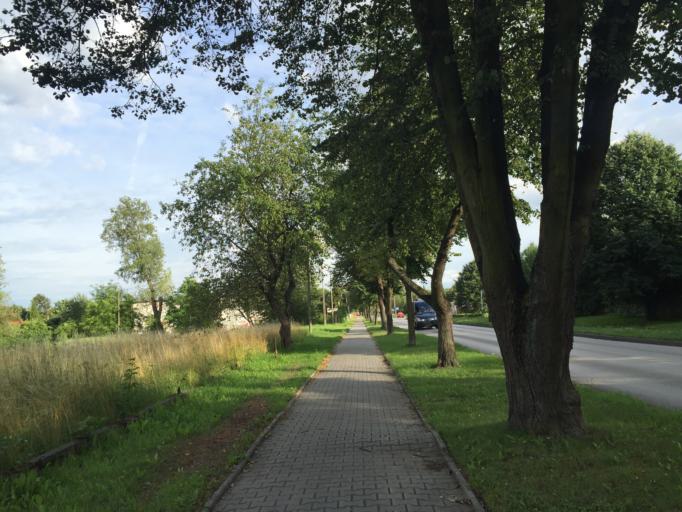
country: PL
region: Lesser Poland Voivodeship
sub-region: Powiat oswiecimski
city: Brzezinka
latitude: 50.0338
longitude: 19.1968
